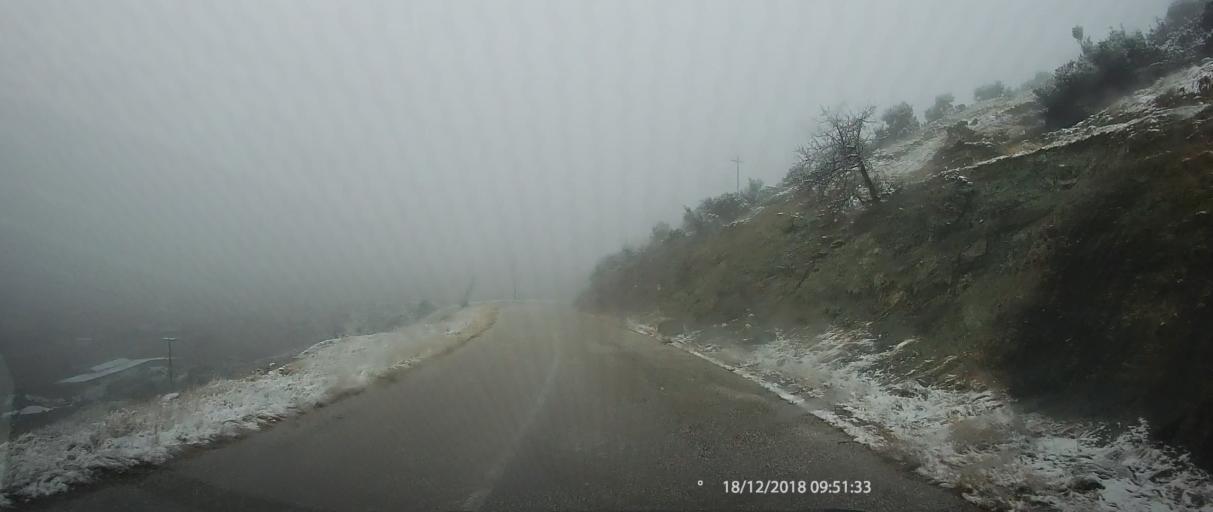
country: GR
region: Thessaly
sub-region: Nomos Larisis
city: Livadi
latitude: 40.0295
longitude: 22.2513
